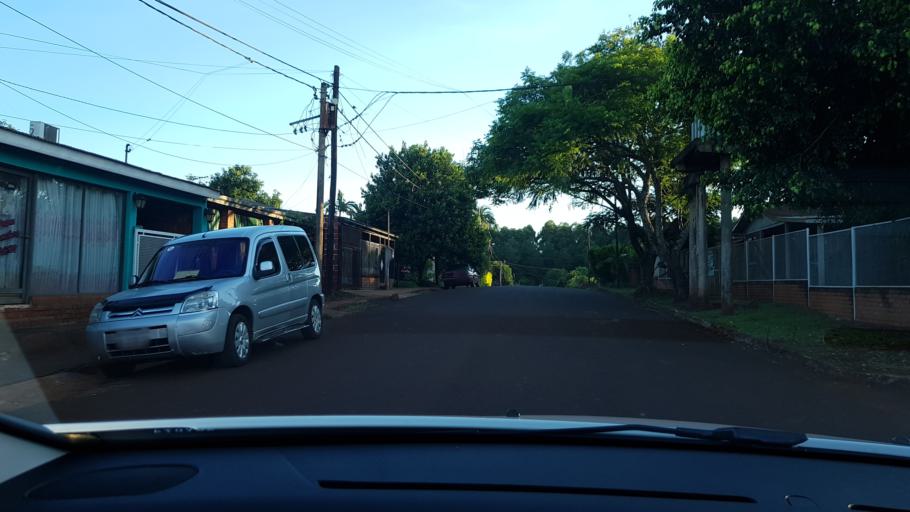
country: AR
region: Misiones
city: Puerto Libertad
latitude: -25.9230
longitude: -54.5816
